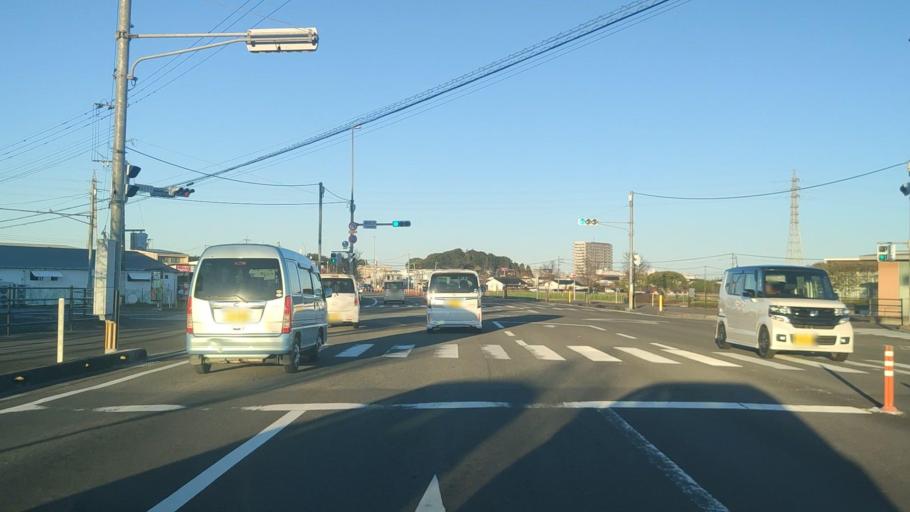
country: JP
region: Miyazaki
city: Miyazaki-shi
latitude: 31.8923
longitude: 131.4058
